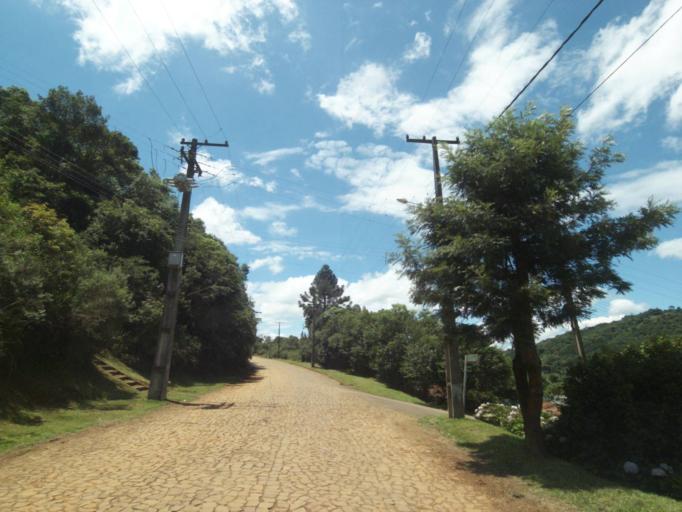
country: BR
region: Parana
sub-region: Uniao Da Vitoria
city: Uniao da Vitoria
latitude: -26.1644
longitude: -51.5563
